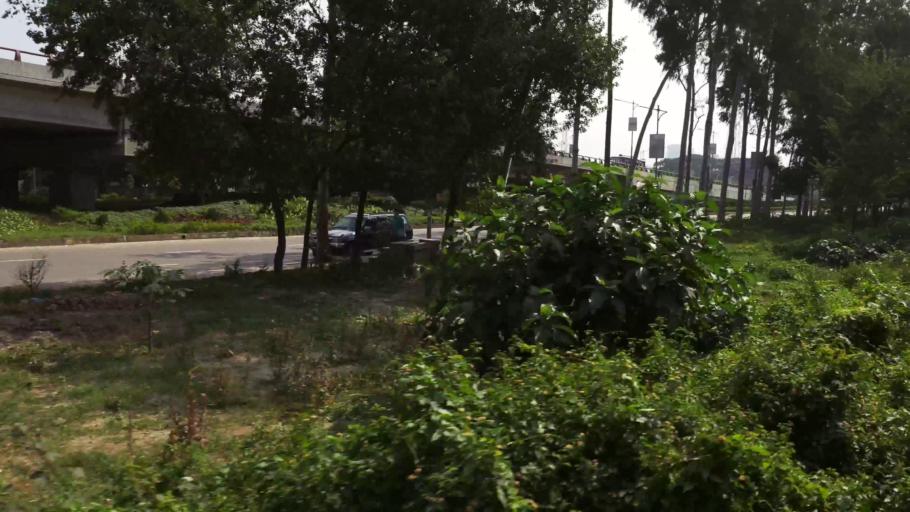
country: BD
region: Dhaka
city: Tungi
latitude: 23.8420
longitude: 90.4166
